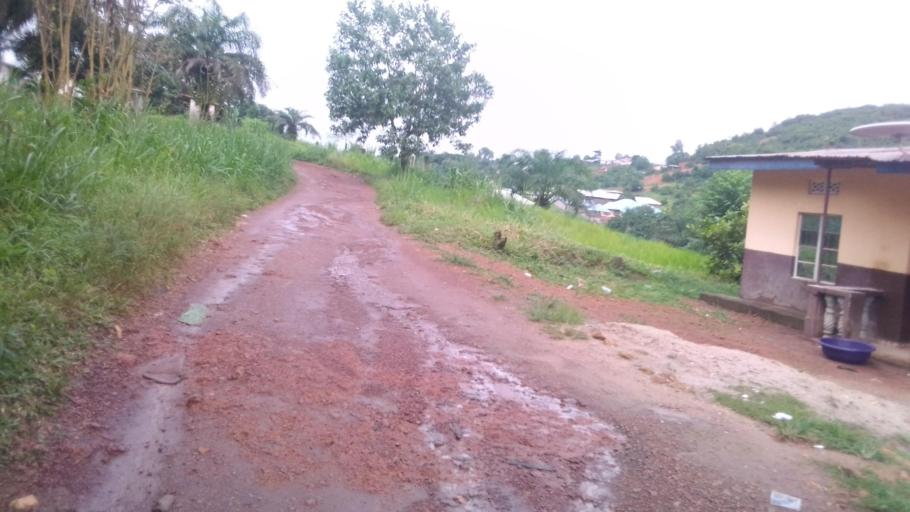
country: SL
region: Eastern Province
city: Kenema
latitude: 7.8521
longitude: -11.1953
